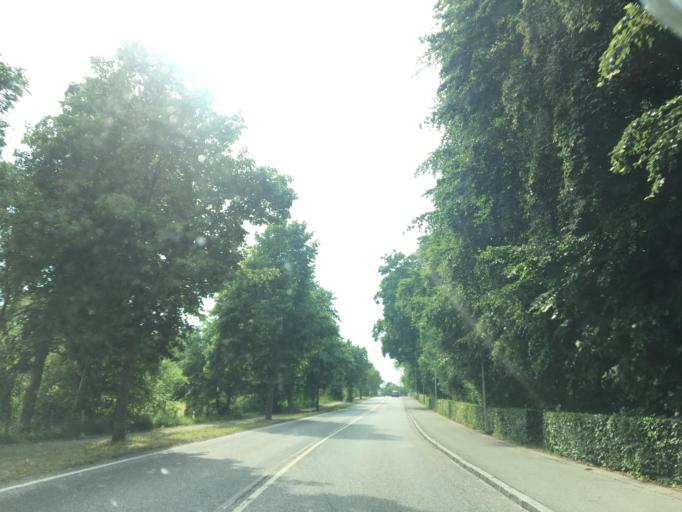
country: DK
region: Zealand
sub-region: Greve Kommune
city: Tune
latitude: 55.5974
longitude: 12.2200
